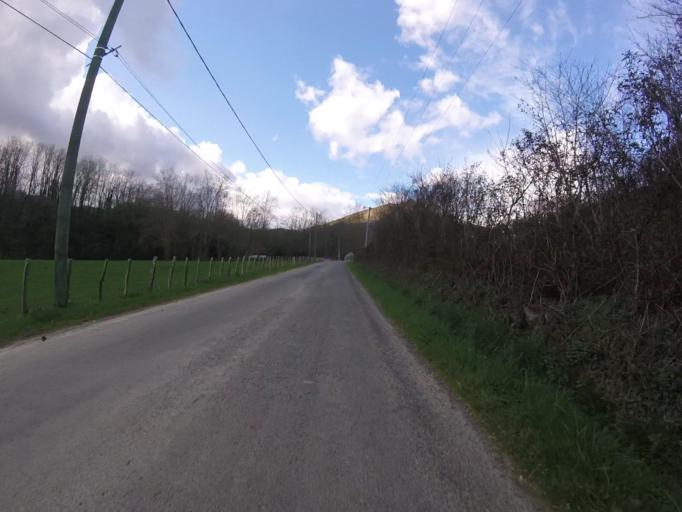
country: FR
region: Aquitaine
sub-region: Departement des Pyrenees-Atlantiques
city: Sare
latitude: 43.2821
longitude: -1.5905
